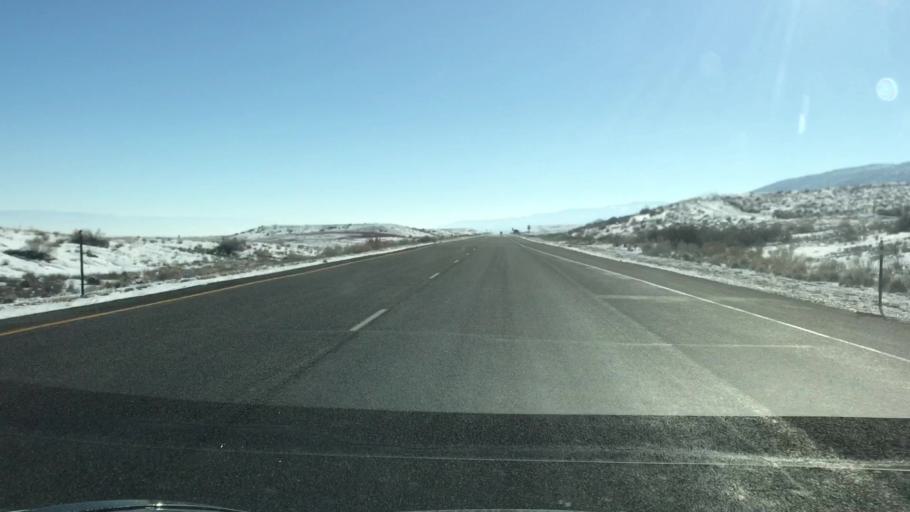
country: US
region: Colorado
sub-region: Mesa County
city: Loma
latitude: 39.2100
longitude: -108.8639
